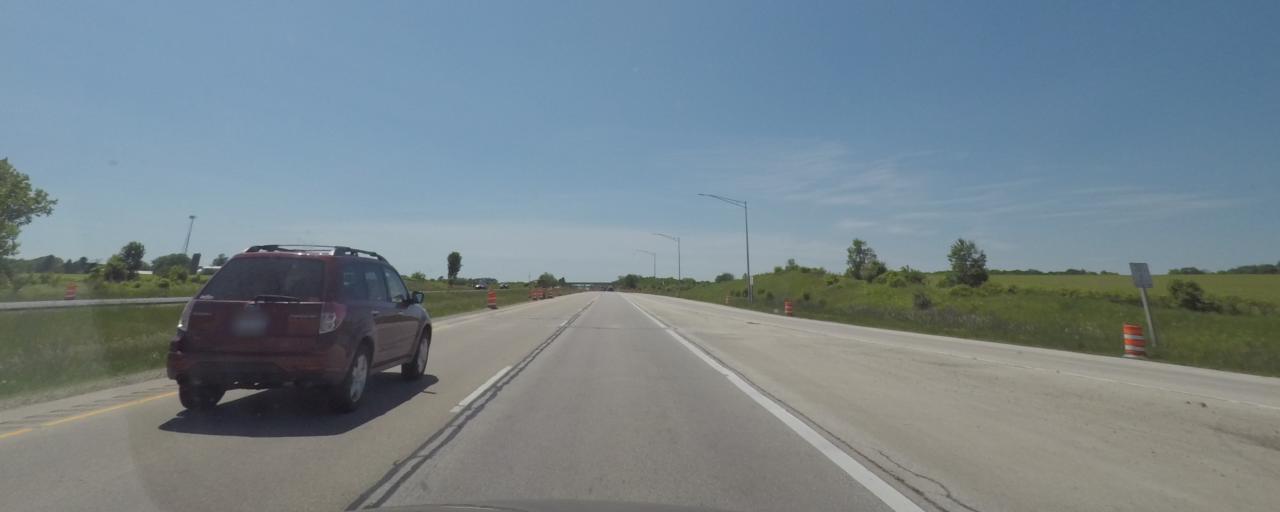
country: US
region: Wisconsin
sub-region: Jefferson County
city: Johnson Creek
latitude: 43.0866
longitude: -88.8272
